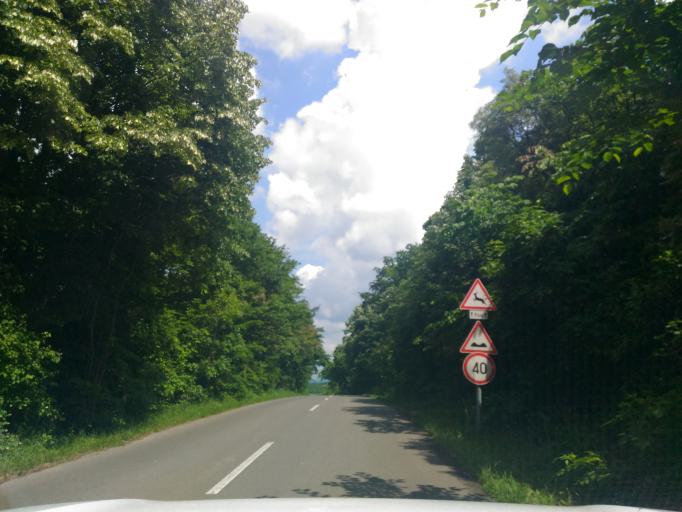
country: HU
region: Baranya
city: Pecs
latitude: 46.1149
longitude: 18.1984
